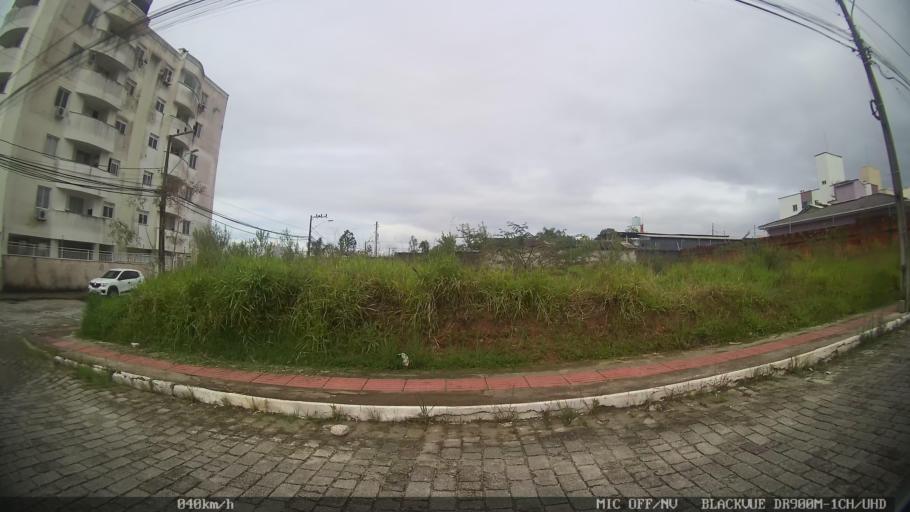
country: BR
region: Santa Catarina
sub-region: Sao Jose
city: Campinas
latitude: -27.5522
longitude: -48.6361
